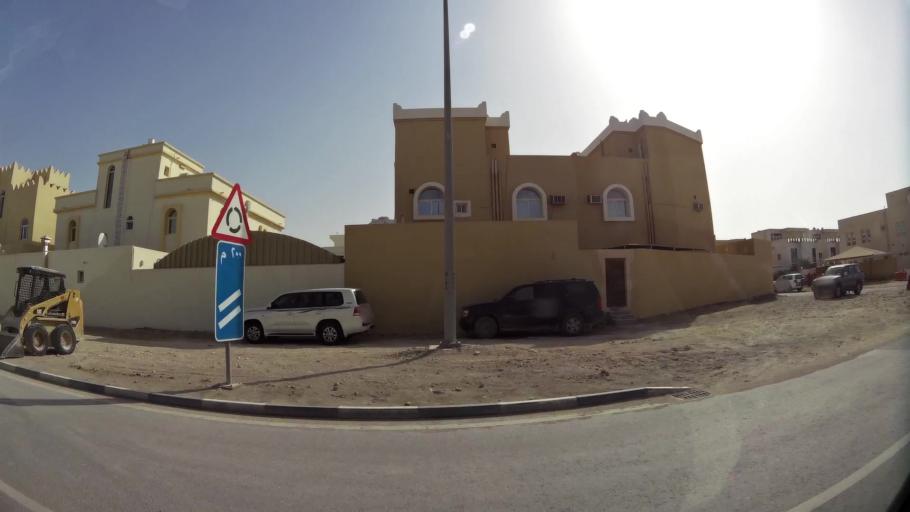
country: QA
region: Baladiyat ar Rayyan
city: Ar Rayyan
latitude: 25.3404
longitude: 51.4237
